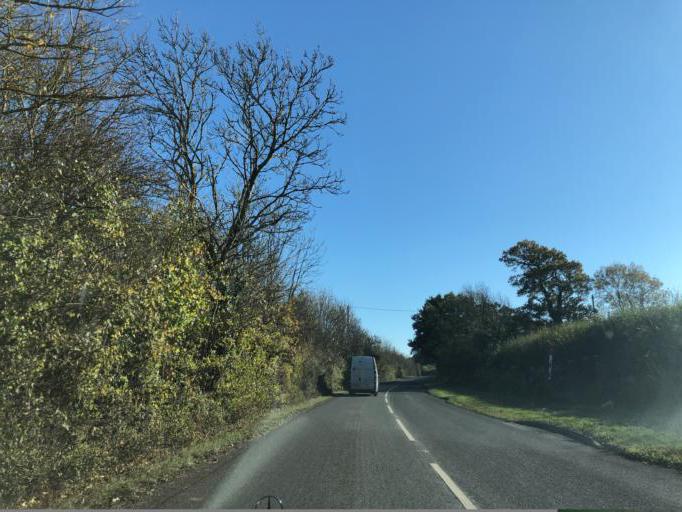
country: GB
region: England
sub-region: Warwickshire
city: Royal Leamington Spa
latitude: 52.2529
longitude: -1.5208
